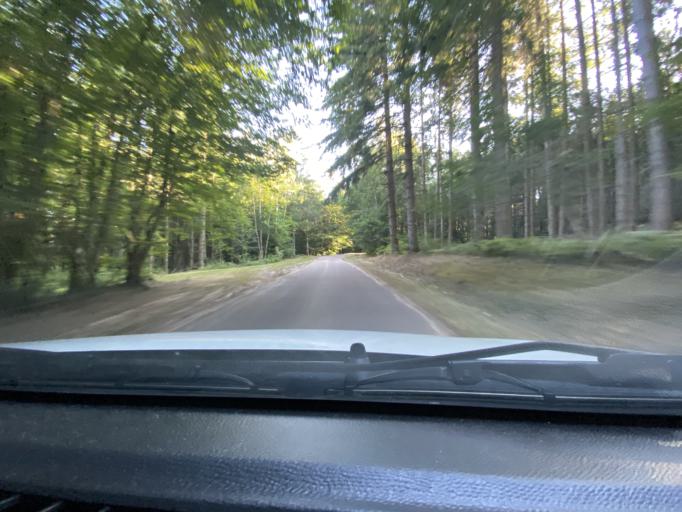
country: FR
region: Bourgogne
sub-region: Departement de la Cote-d'Or
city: Saulieu
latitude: 47.2961
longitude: 4.1742
